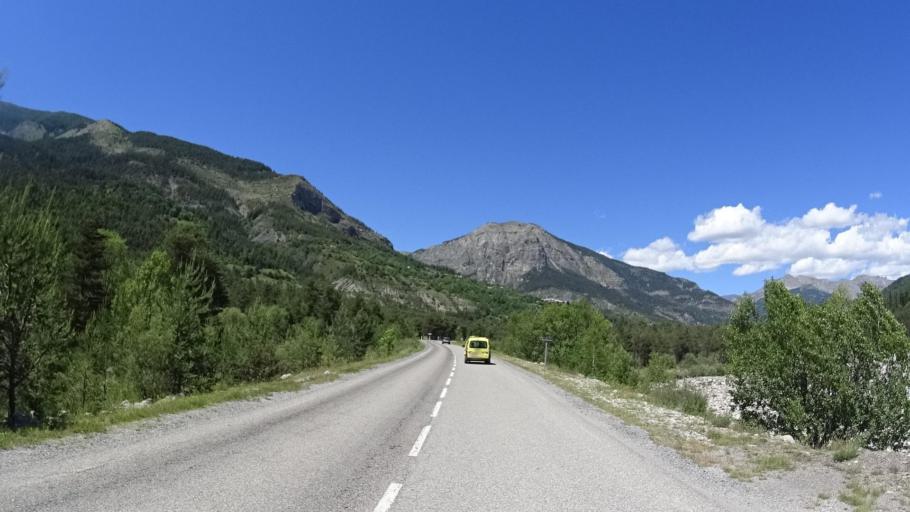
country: FR
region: Provence-Alpes-Cote d'Azur
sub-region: Departement des Alpes-de-Haute-Provence
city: Annot
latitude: 44.1507
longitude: 6.5986
